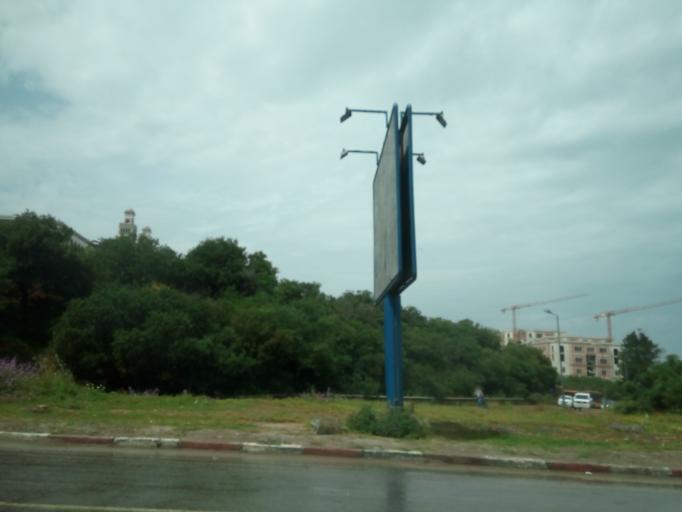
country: DZ
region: Alger
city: Bab Ezzouar
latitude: 36.7333
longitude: 3.1195
